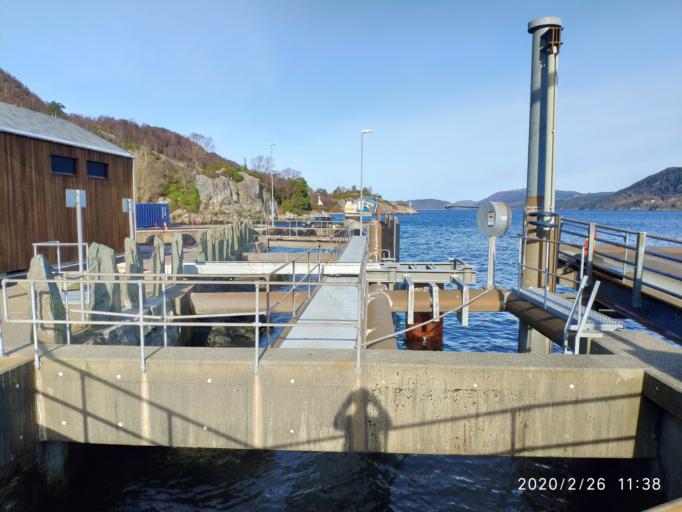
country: NO
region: Hordaland
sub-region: Stord
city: Leirvik
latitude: 59.8861
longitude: 5.5215
